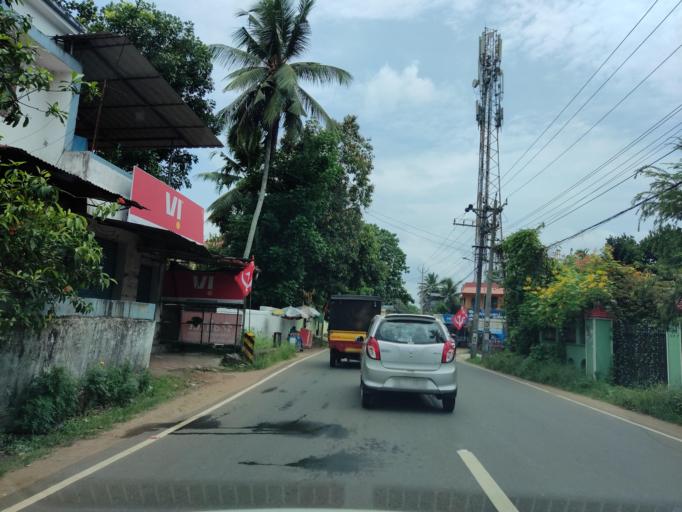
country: IN
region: Kerala
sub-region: Pattanamtitta
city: Adur
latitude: 9.2245
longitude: 76.6721
